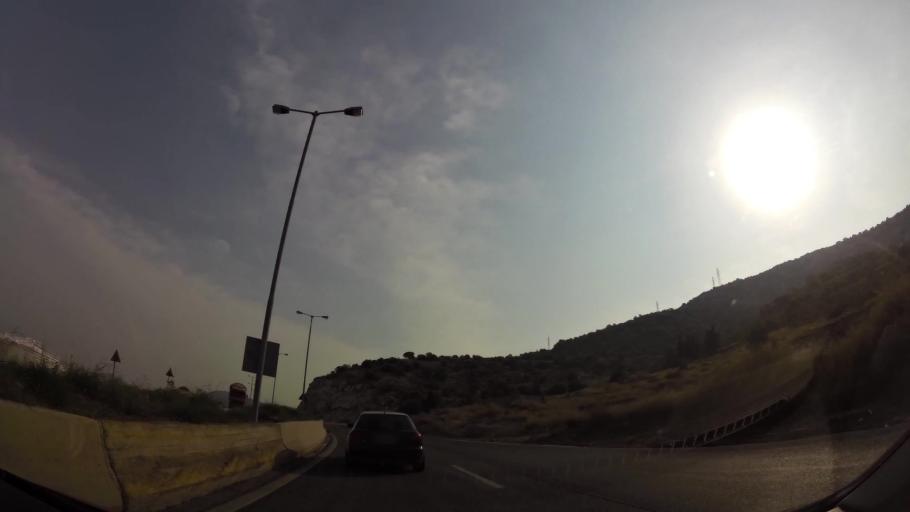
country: GR
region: Attica
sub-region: Nomarchia Athinas
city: Skaramangas
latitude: 38.0256
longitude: 23.6134
